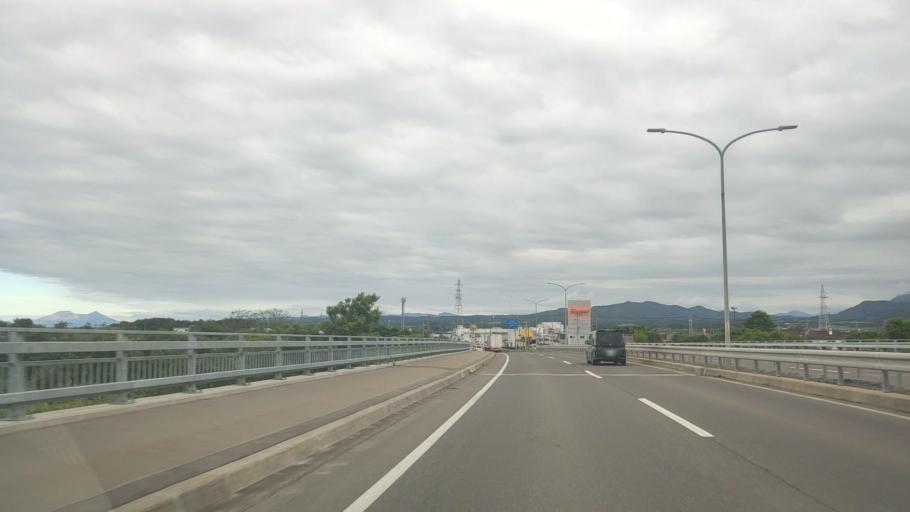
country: JP
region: Hokkaido
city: Nanae
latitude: 42.2633
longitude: 140.2736
